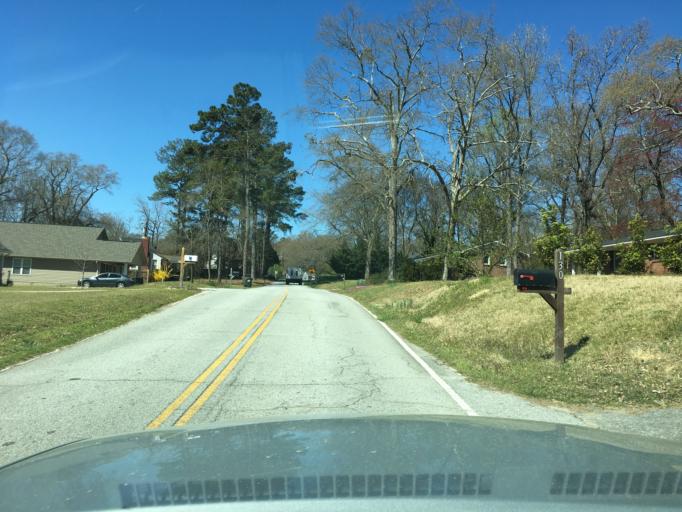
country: US
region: South Carolina
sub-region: Spartanburg County
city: Spartanburg
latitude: 34.9344
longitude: -81.8822
